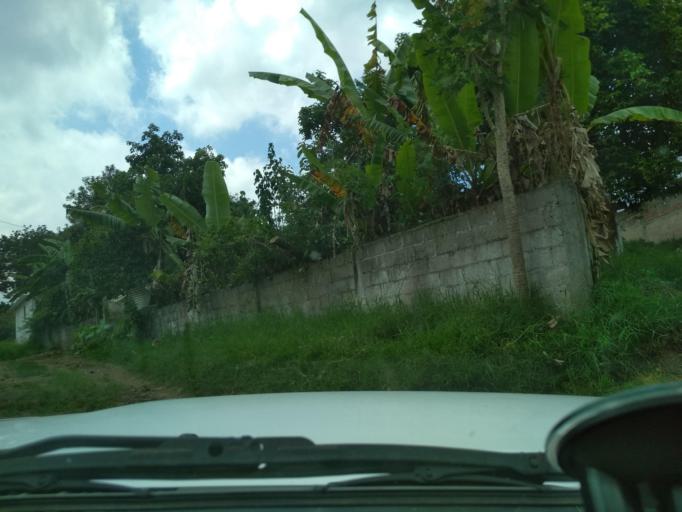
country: MX
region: Veracruz
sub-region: Fortin
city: Monte Salas
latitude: 18.9333
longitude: -97.0168
